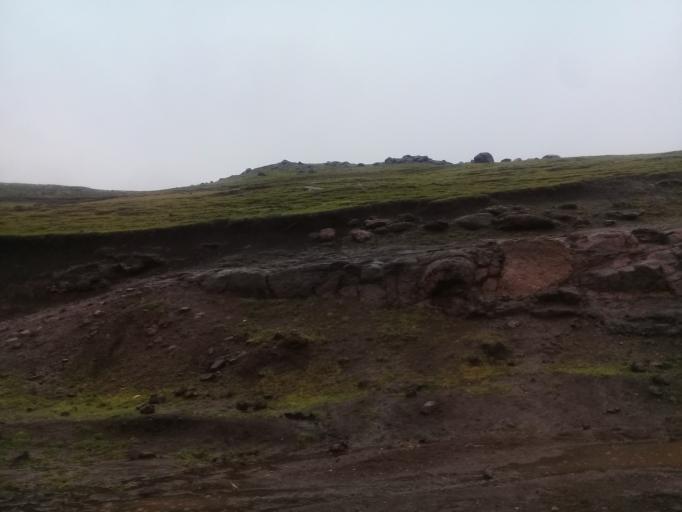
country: LS
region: Mokhotlong
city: Mokhotlong
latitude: -29.3879
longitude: 28.9545
